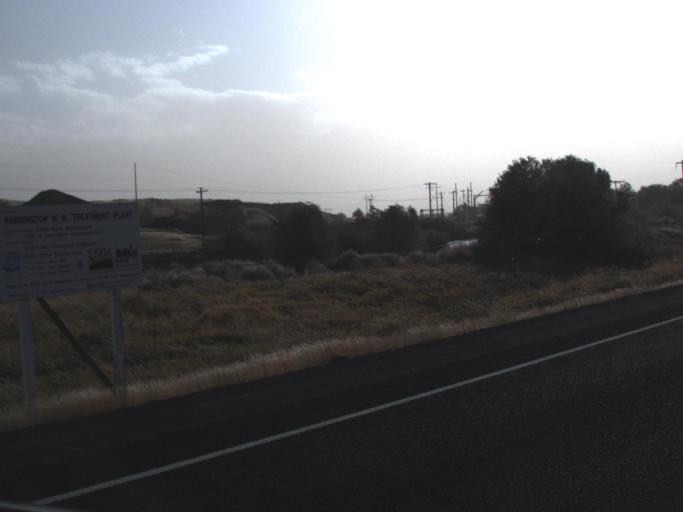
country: US
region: Washington
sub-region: Lincoln County
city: Davenport
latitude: 47.4798
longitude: -118.2623
